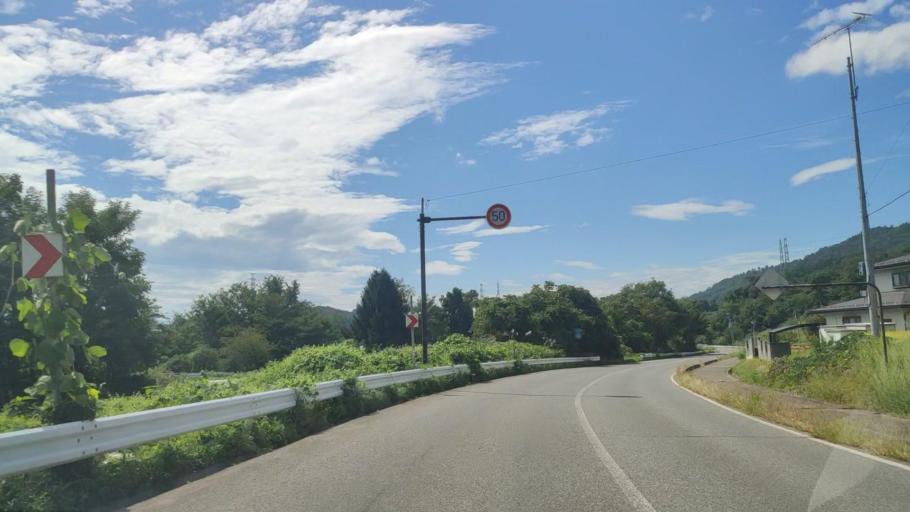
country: JP
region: Nagano
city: Nakano
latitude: 36.7421
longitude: 138.3085
